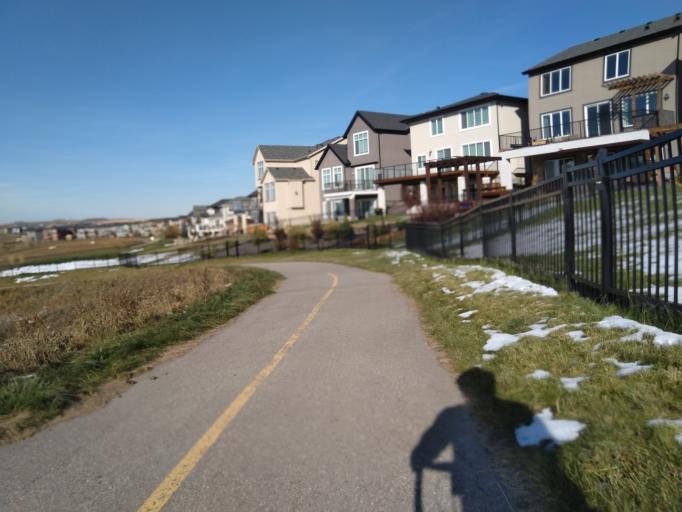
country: CA
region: Alberta
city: Calgary
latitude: 51.1719
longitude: -114.1235
